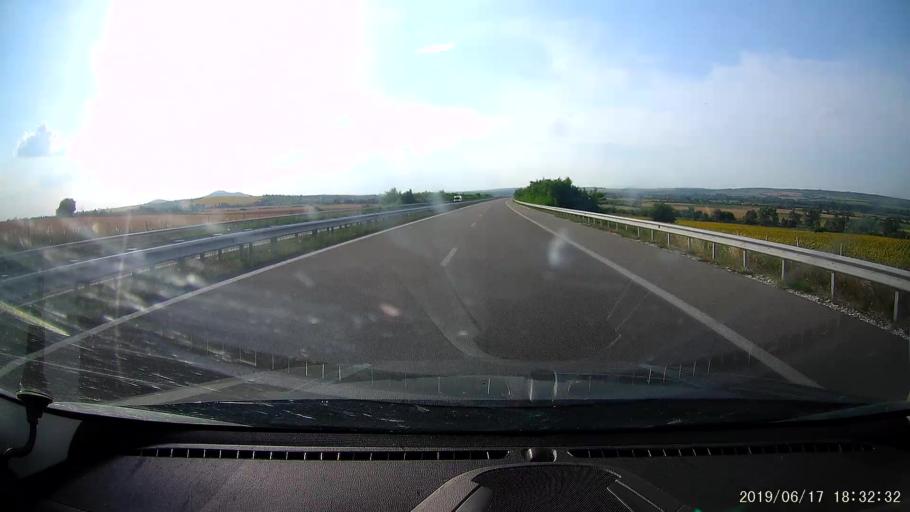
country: BG
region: Khaskovo
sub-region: Obshtina Dimitrovgrad
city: Dimitrovgrad
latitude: 42.0613
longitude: 25.4767
